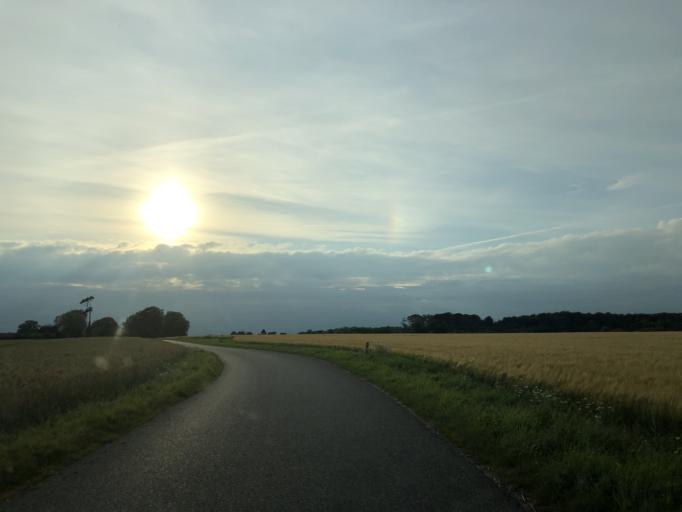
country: DK
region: South Denmark
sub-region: Fredericia Kommune
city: Taulov
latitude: 55.5954
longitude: 9.6091
